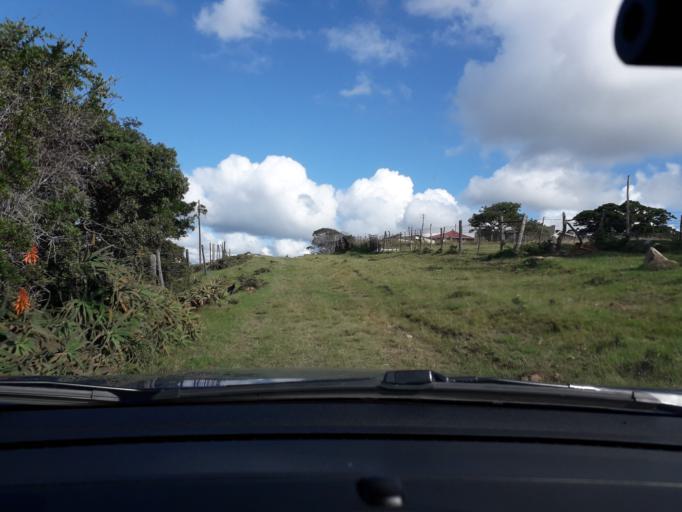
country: ZA
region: Eastern Cape
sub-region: Buffalo City Metropolitan Municipality
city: Bhisho
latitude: -33.1126
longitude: 27.4308
